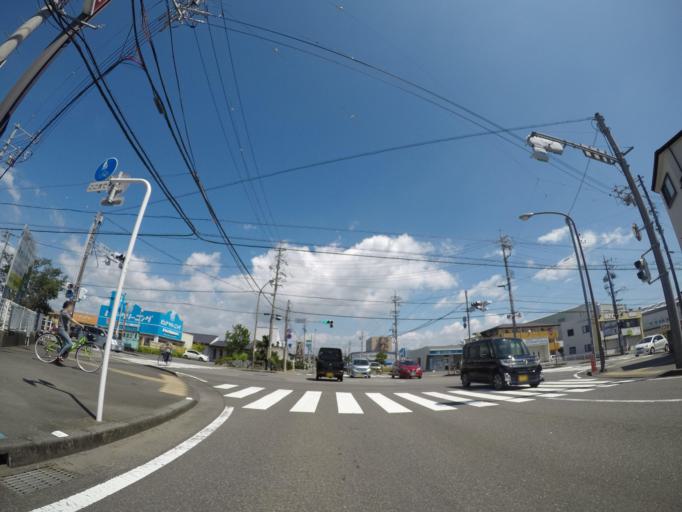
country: JP
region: Shizuoka
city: Fujieda
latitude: 34.8533
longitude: 138.2888
